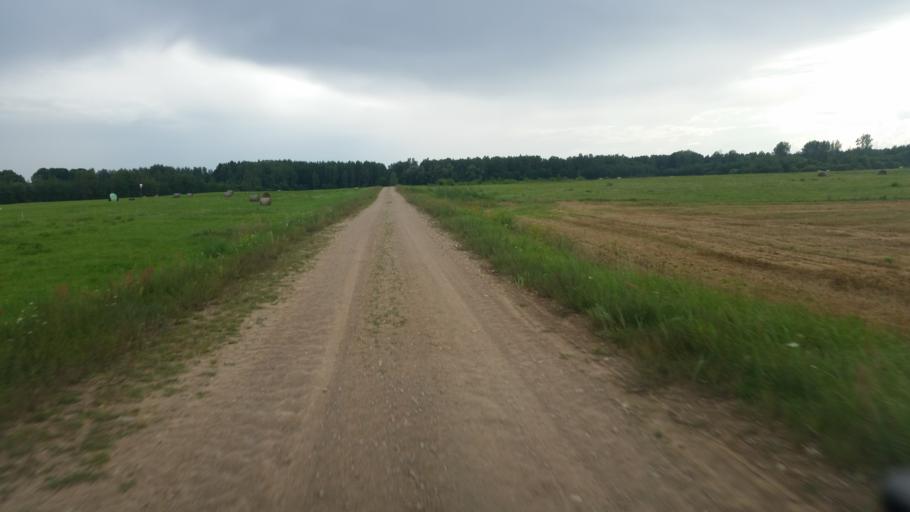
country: LV
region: Vecumnieki
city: Vecumnieki
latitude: 56.4469
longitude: 24.6377
